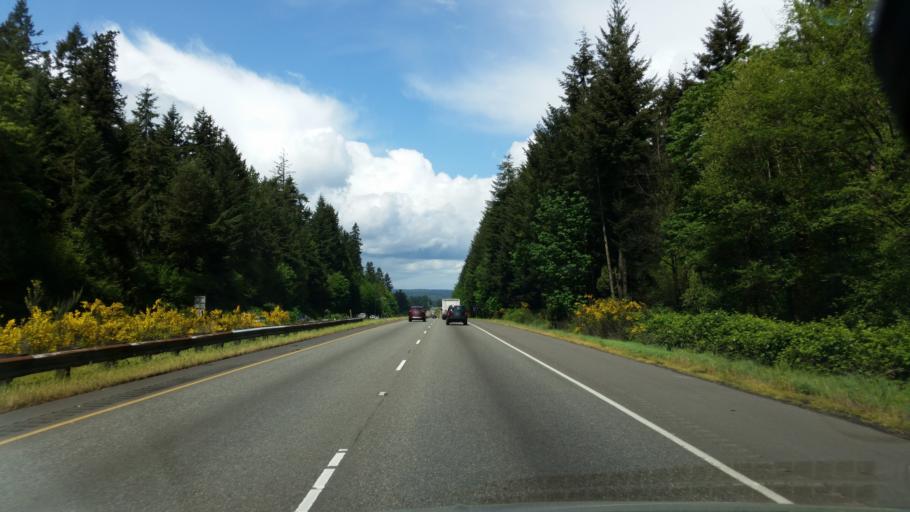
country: US
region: Washington
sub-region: Pierce County
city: Canterwood
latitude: 47.3489
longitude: -122.6105
